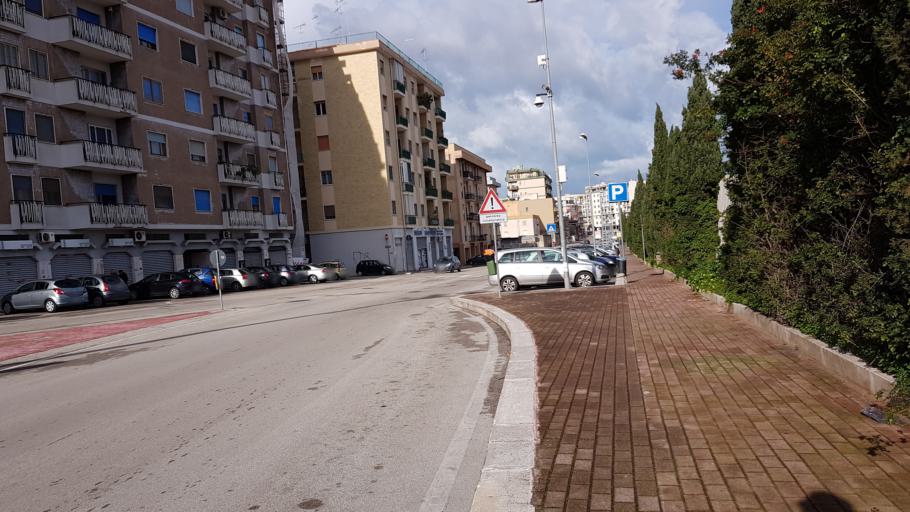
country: IT
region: Apulia
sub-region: Provincia di Brindisi
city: Brindisi
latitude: 40.6328
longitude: 17.9391
